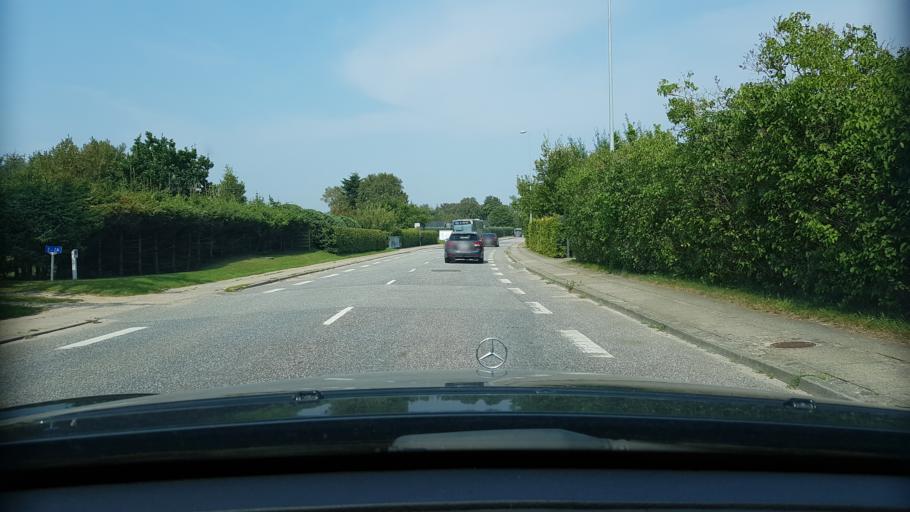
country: DK
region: North Denmark
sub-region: Mariagerfjord Kommune
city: Hadsund
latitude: 56.8088
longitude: 10.2703
